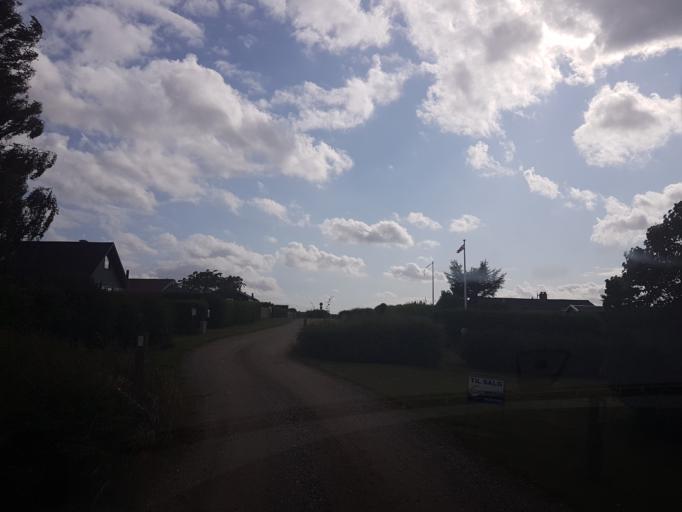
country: DK
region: South Denmark
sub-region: Middelfart Kommune
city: Brenderup
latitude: 55.5339
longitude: 10.0054
